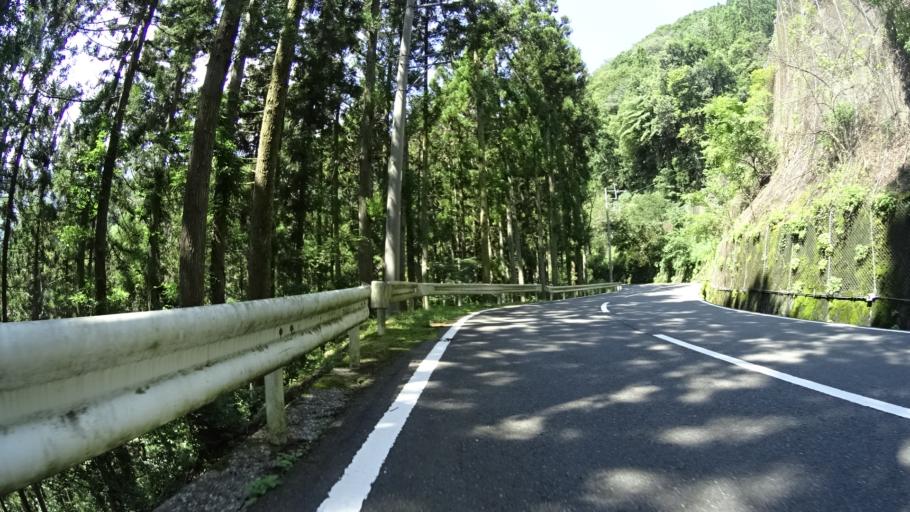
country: JP
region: Gunma
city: Tomioka
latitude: 36.0597
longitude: 138.8470
